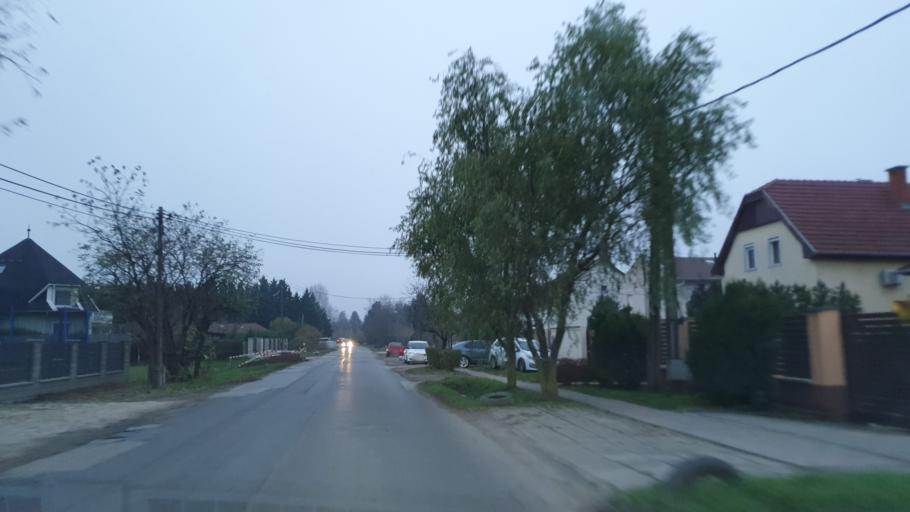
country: HU
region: Pest
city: Csomor
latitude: 47.5306
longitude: 19.2230
